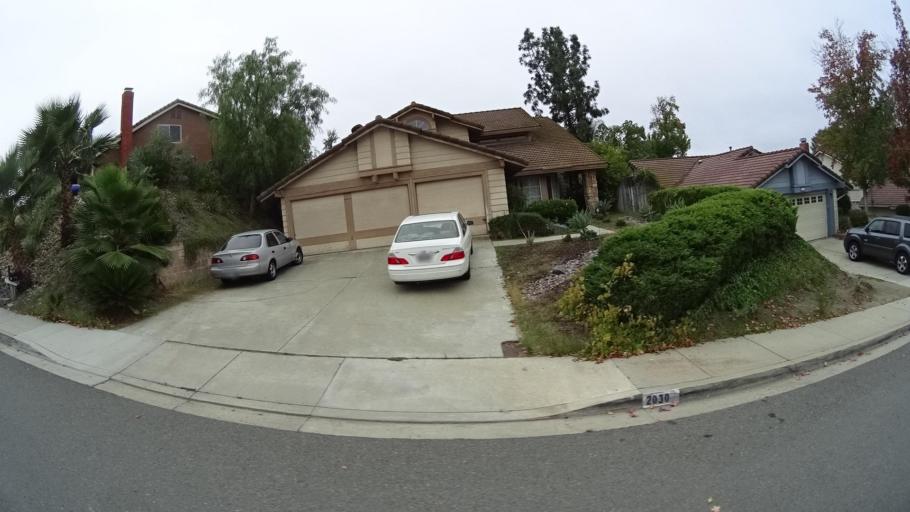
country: US
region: California
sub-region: San Diego County
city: Rancho San Diego
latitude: 32.7574
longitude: -116.9100
